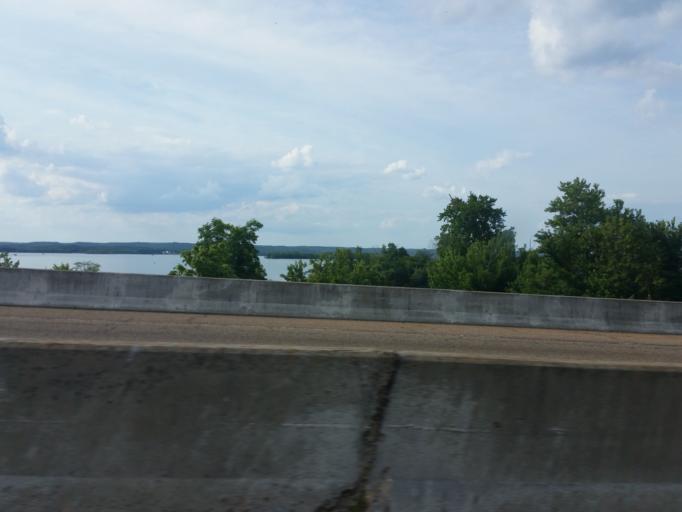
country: US
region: Tennessee
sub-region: Humphreys County
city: New Johnsonville
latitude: 36.0177
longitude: -87.9971
